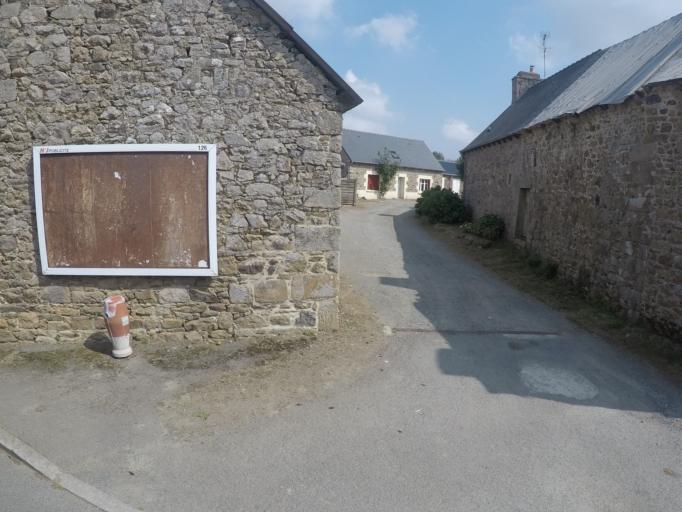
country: FR
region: Brittany
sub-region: Departement des Cotes-d'Armor
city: Saint-Donan
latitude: 48.5059
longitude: -2.9147
